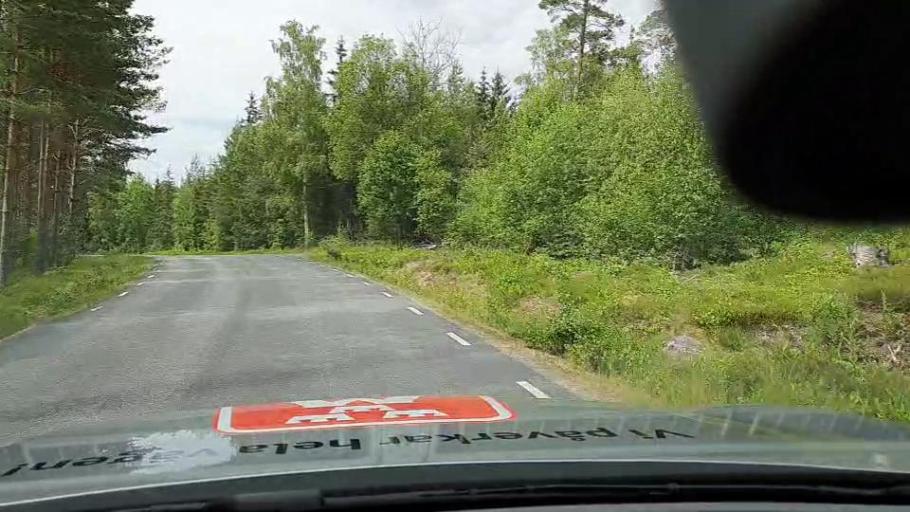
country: SE
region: Soedermanland
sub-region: Eskilstuna Kommun
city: Arla
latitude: 59.2475
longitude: 16.7165
